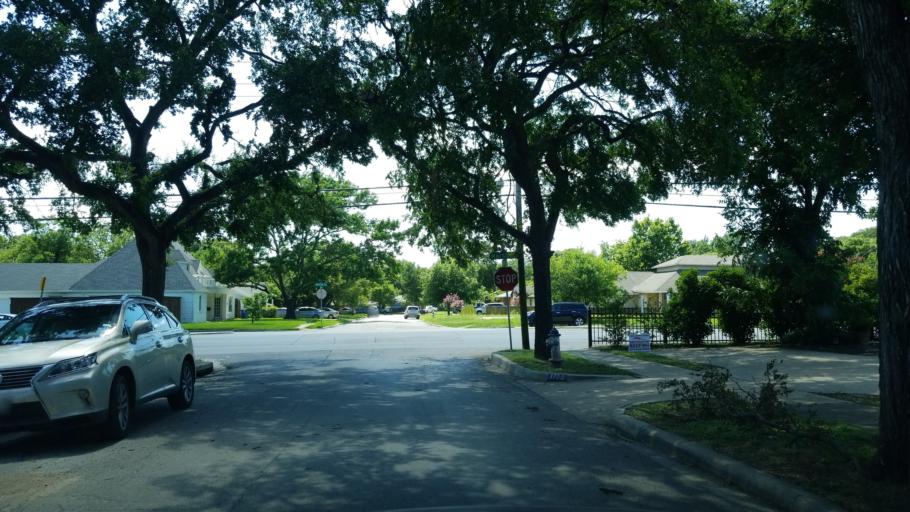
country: US
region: Texas
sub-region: Dallas County
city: University Park
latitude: 32.8786
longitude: -96.8558
